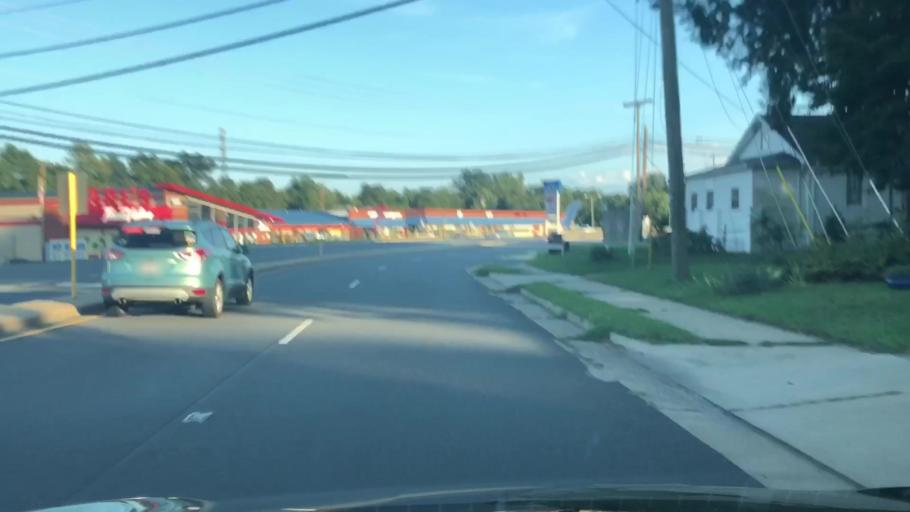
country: US
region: Virginia
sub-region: City of Fredericksburg
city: Fredericksburg
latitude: 38.3112
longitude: -77.4488
